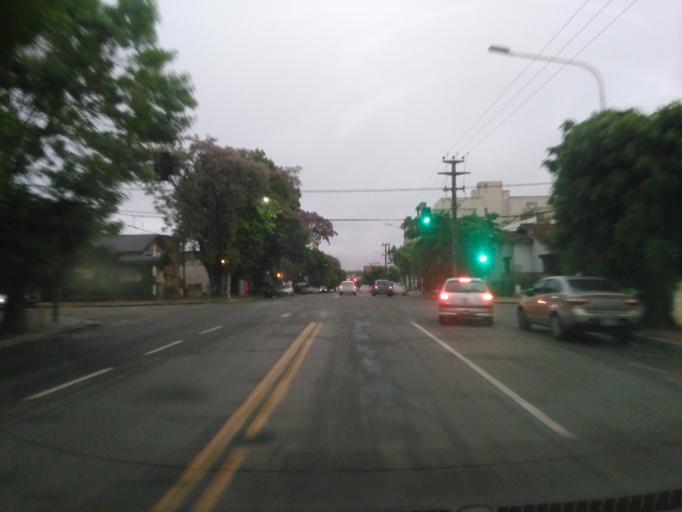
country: AR
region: Buenos Aires
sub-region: Partido de Tandil
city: Tandil
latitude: -37.3309
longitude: -59.1441
